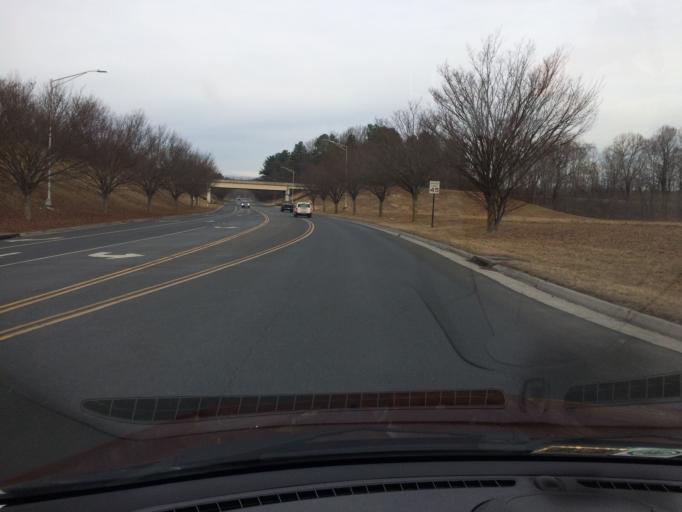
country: US
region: Virginia
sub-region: City of Bedford
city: Bedford
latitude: 37.3380
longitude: -79.4967
